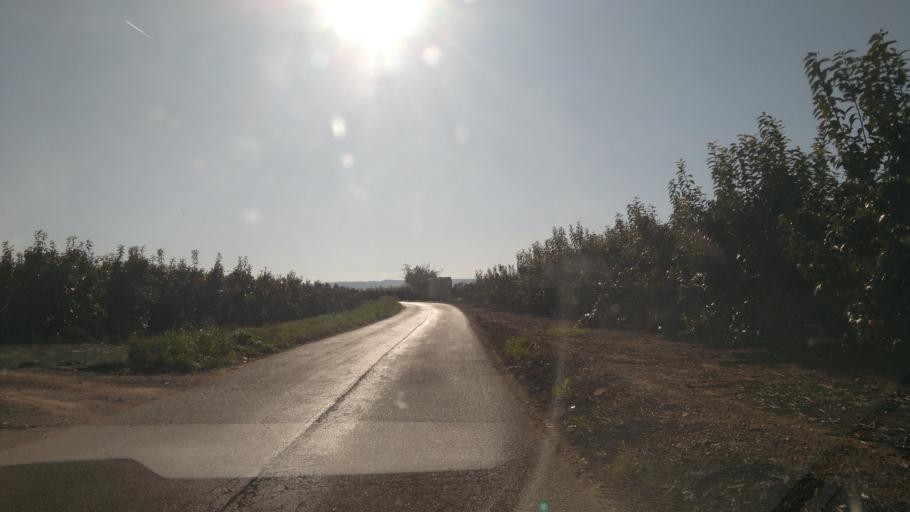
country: ES
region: Valencia
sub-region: Provincia de Valencia
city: L'Alcudia
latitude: 39.1847
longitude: -0.5275
